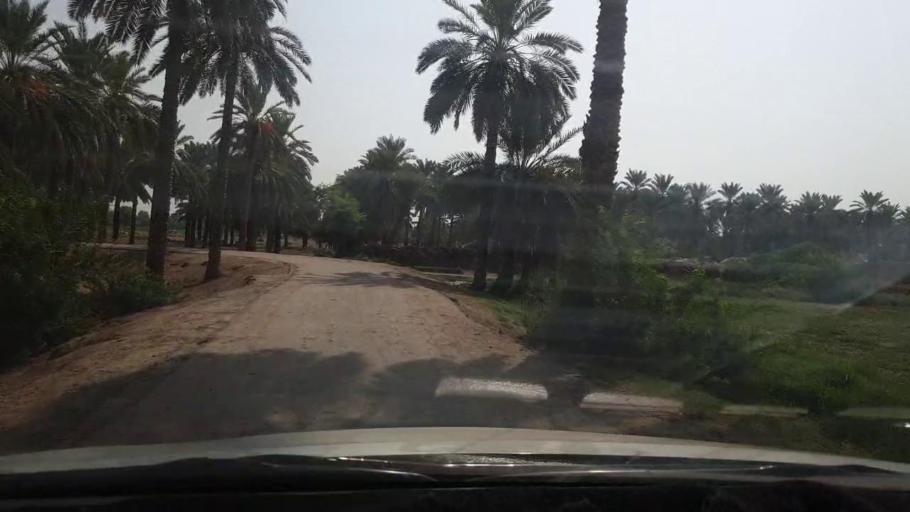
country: PK
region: Sindh
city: Rohri
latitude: 27.6186
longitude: 68.9023
